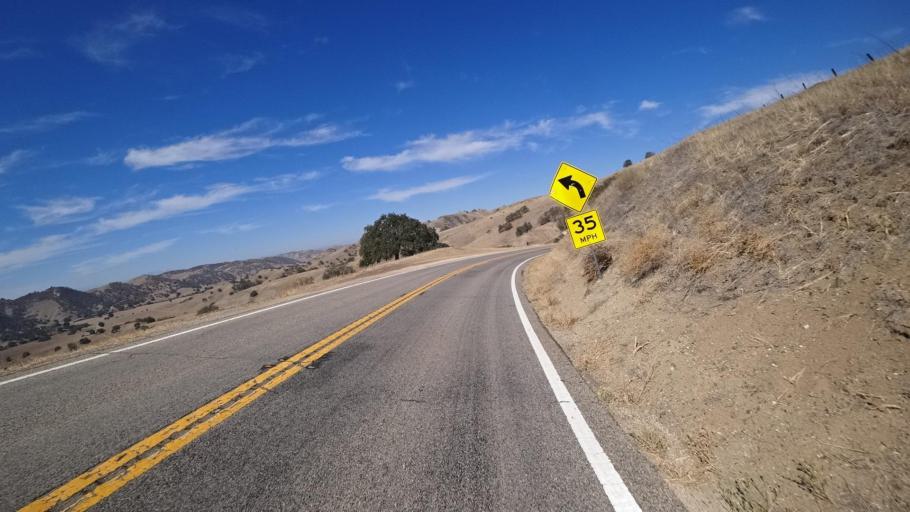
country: US
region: California
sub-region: Monterey County
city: King City
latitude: 36.1902
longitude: -120.8040
